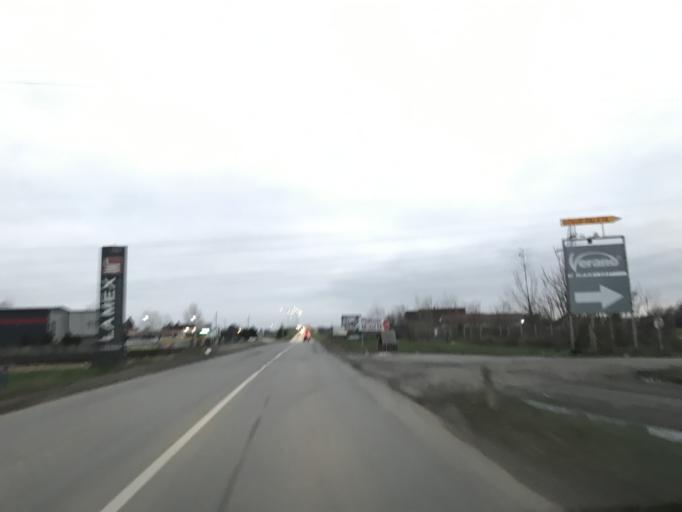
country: RS
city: Veternik
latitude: 45.2826
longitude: 19.7740
